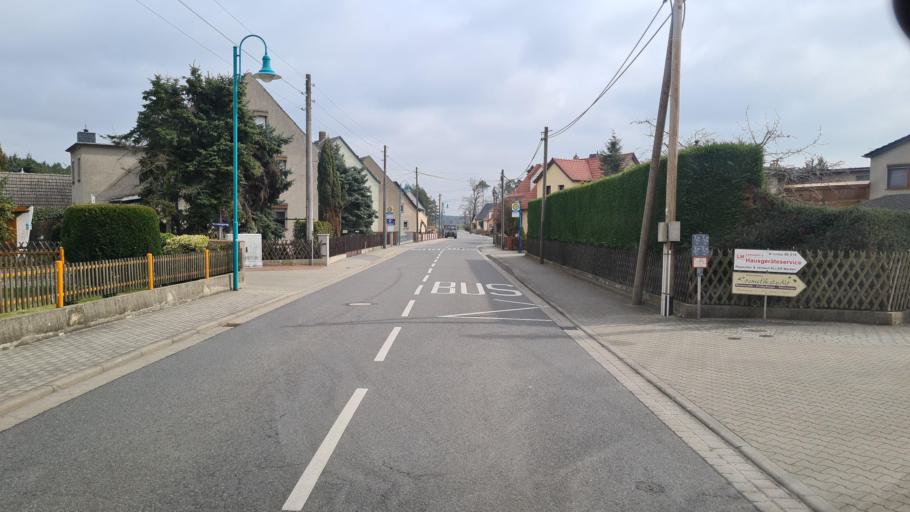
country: DE
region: Saxony
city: Zabeltitz
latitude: 51.3888
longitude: 13.4872
